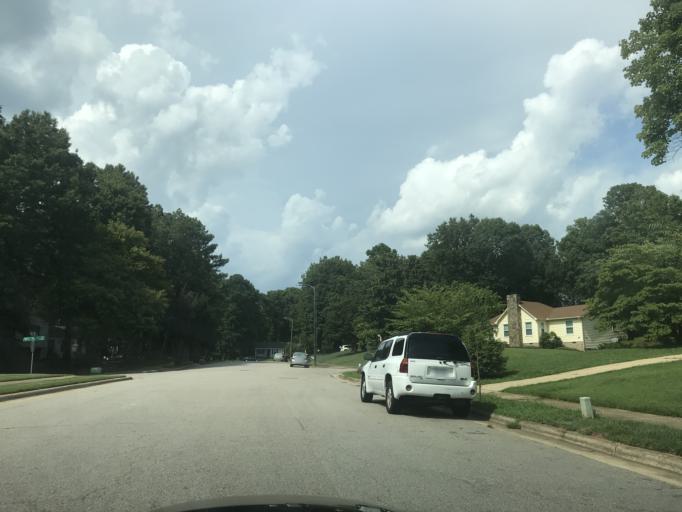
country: US
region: North Carolina
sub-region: Wake County
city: West Raleigh
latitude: 35.8804
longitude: -78.6560
